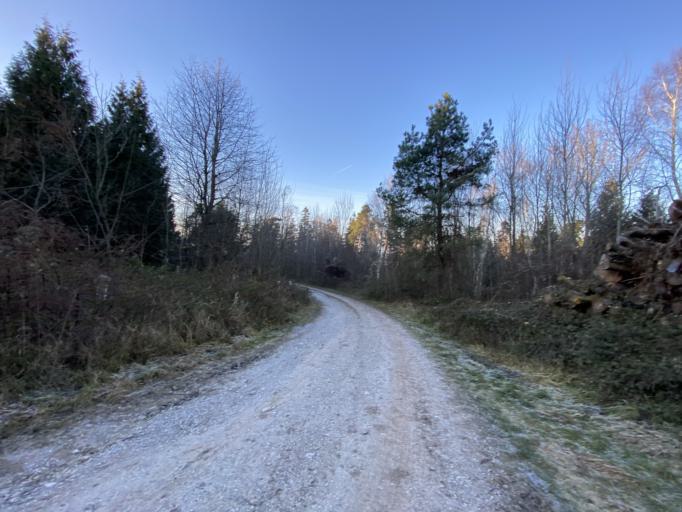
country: AT
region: Lower Austria
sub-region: Politischer Bezirk Sankt Polten
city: Boheimkirchen
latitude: 48.2152
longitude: 15.7140
